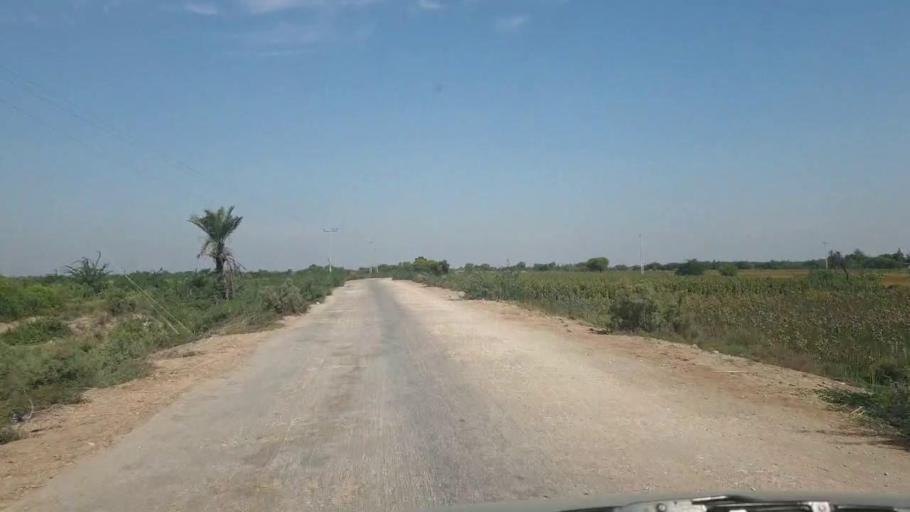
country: PK
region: Sindh
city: Tando Bago
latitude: 24.8702
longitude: 68.9982
